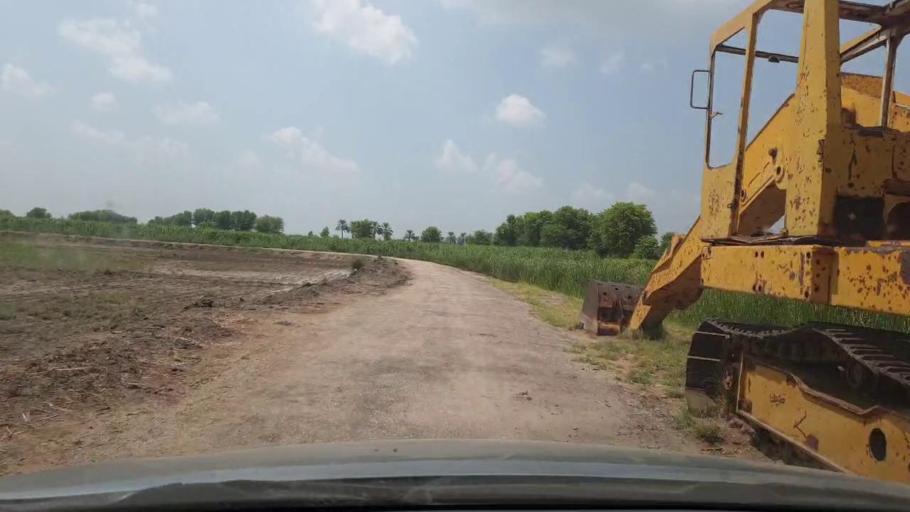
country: PK
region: Sindh
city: Kot Diji
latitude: 27.3950
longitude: 68.7254
